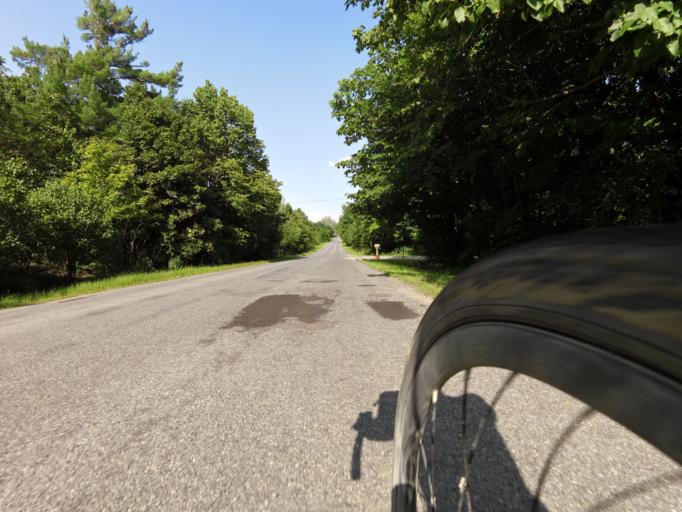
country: CA
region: Ontario
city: Kingston
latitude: 44.3457
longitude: -76.6520
